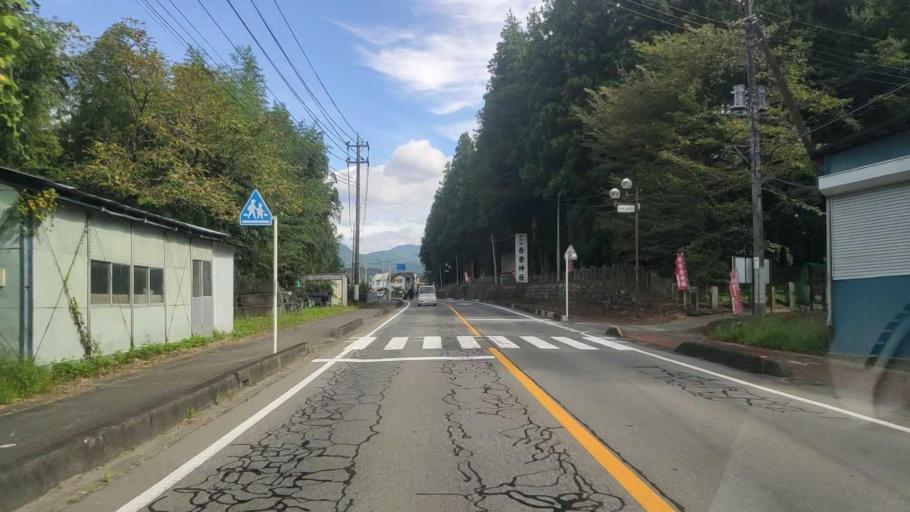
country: JP
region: Gunma
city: Nakanojomachi
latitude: 36.5912
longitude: 138.8609
